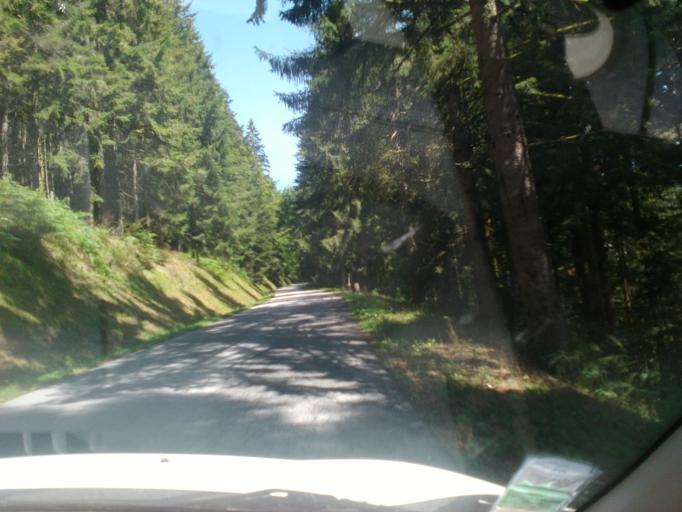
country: FR
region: Lorraine
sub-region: Departement des Vosges
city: Le Tholy
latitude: 48.0330
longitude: 6.7688
